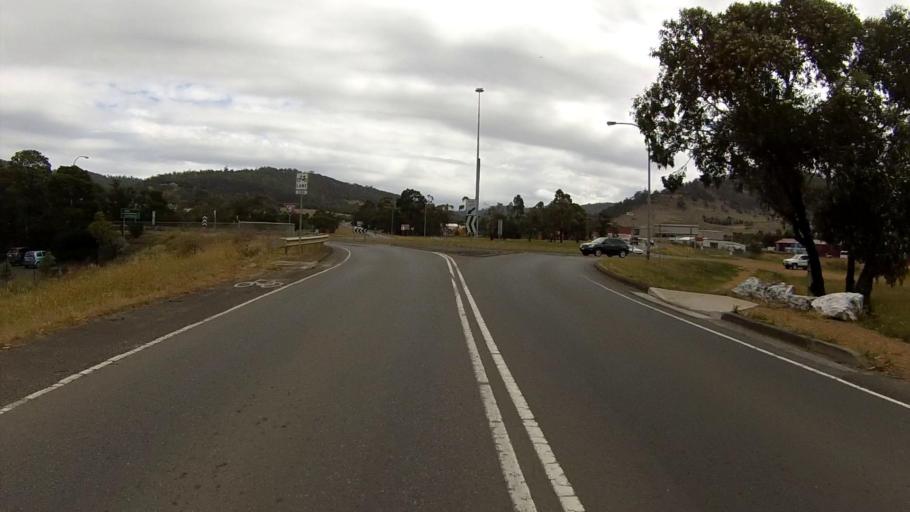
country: AU
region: Tasmania
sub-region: Clarence
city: Cambridge
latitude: -42.8337
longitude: 147.4563
